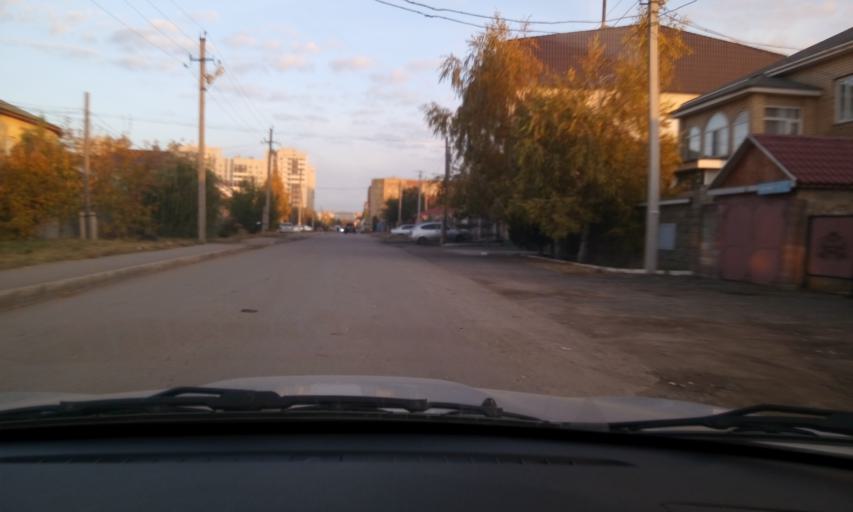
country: KZ
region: Astana Qalasy
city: Astana
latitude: 51.1370
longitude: 71.4880
